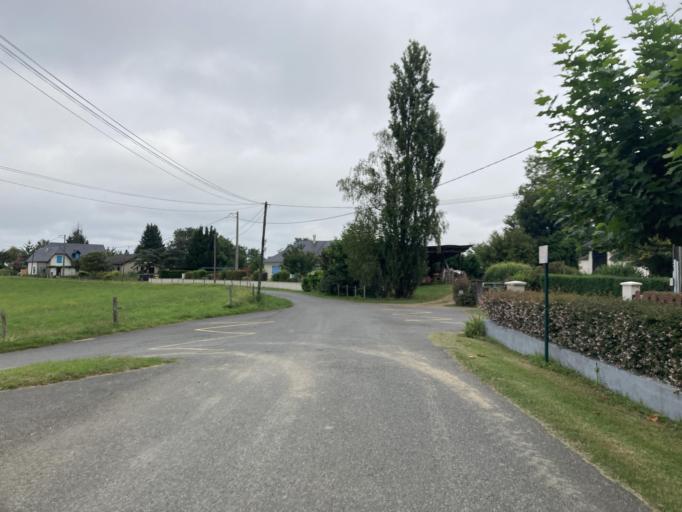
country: FR
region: Aquitaine
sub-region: Departement des Pyrenees-Atlantiques
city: Ledeuix
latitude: 43.2653
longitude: -0.6297
